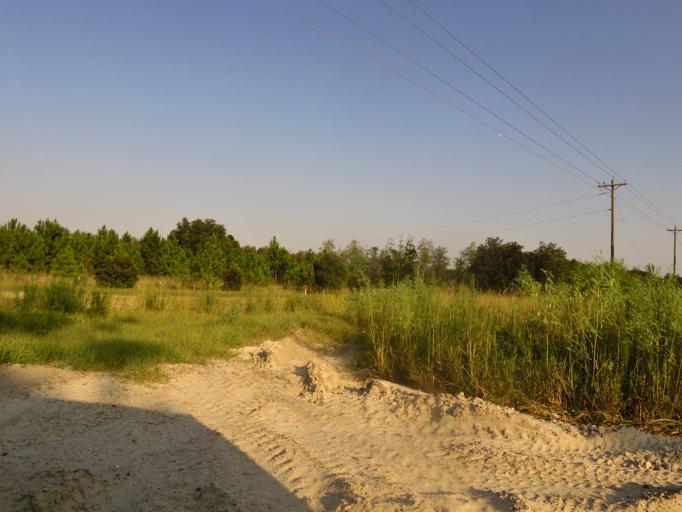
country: US
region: Florida
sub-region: Nassau County
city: Hilliard
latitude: 30.5553
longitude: -81.9925
